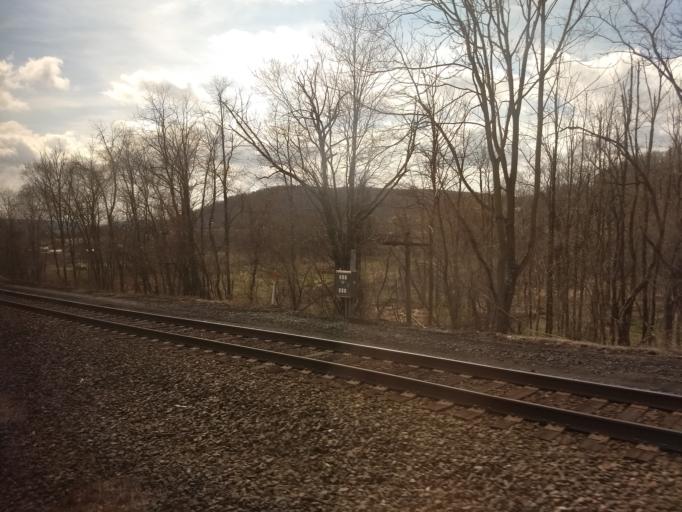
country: US
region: Pennsylvania
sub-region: Huntingdon County
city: Mount Union
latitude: 40.3898
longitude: -77.8880
